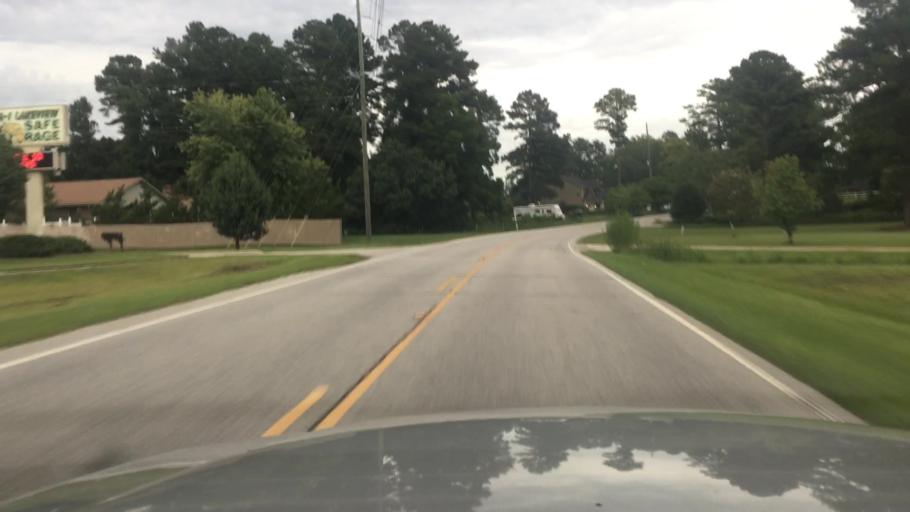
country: US
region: North Carolina
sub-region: Hoke County
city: Rockfish
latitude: 34.9817
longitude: -79.0469
